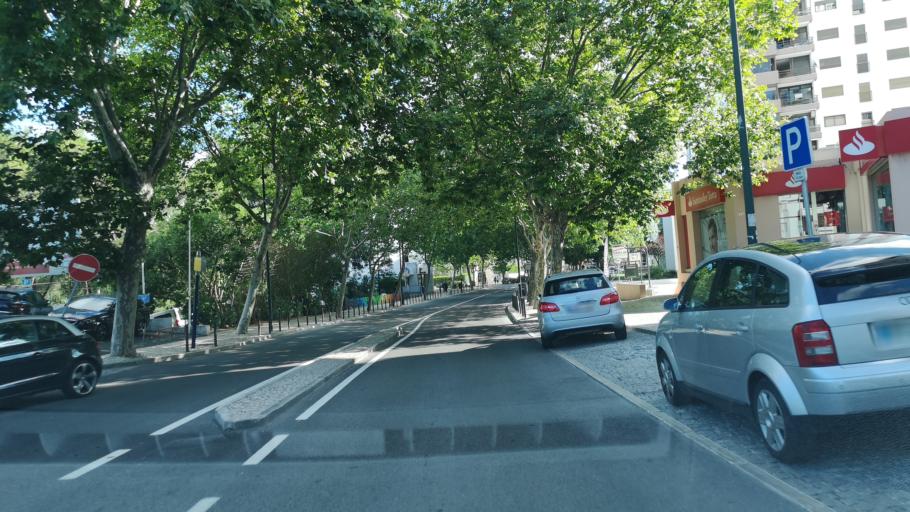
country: PT
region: Lisbon
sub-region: Cascais
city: Cascais
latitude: 38.6965
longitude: -9.4300
